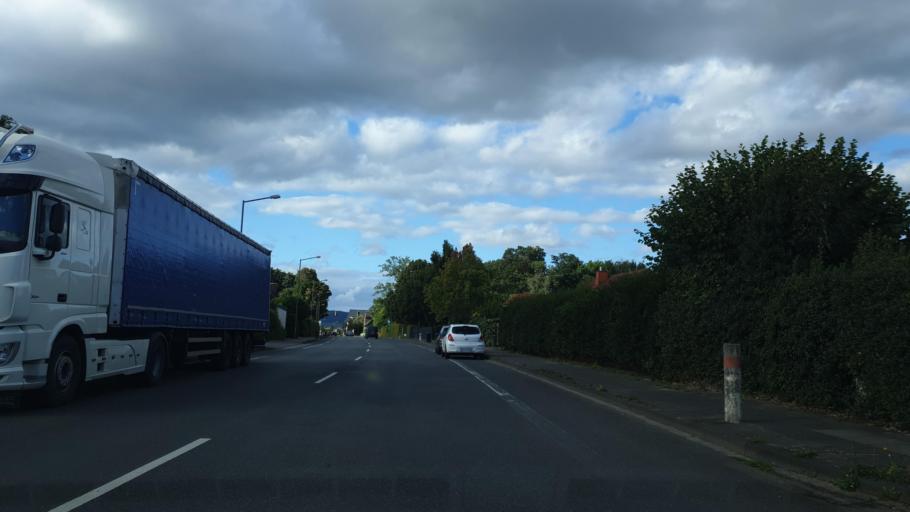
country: DE
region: North Rhine-Westphalia
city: Loehne
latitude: 52.2357
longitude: 8.7037
